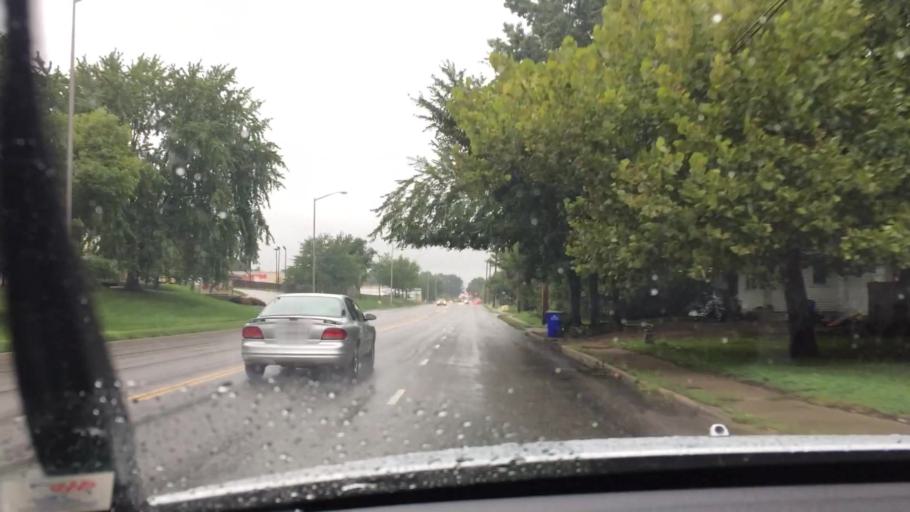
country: US
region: Kansas
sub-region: Johnson County
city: Overland Park
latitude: 38.9932
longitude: -94.6611
